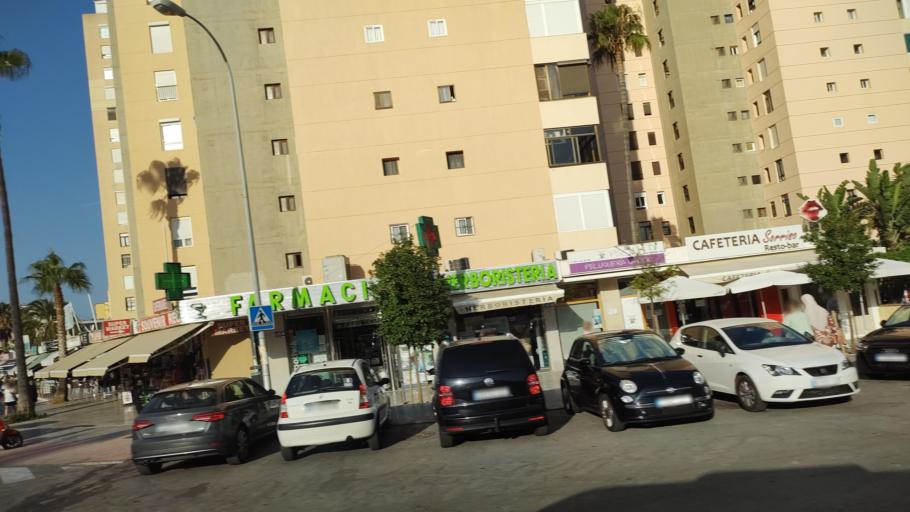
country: ES
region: Andalusia
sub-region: Provincia de Malaga
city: Torremolinos
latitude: 36.6312
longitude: -4.4932
